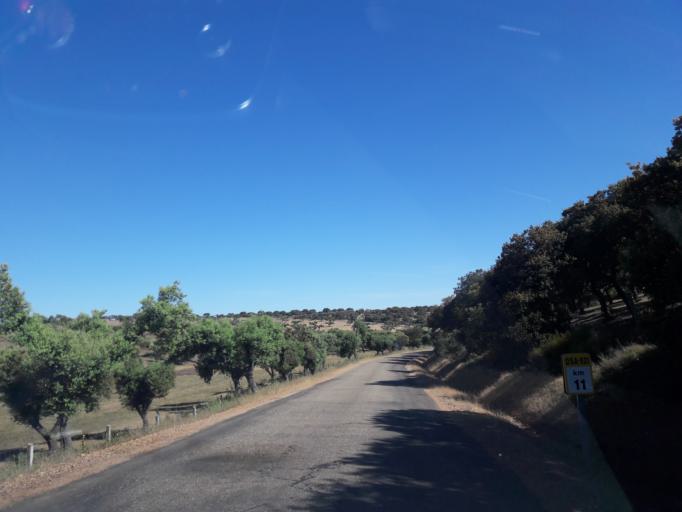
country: ES
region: Castille and Leon
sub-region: Provincia de Salamanca
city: Vega de Tirados
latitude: 41.0544
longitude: -5.8908
